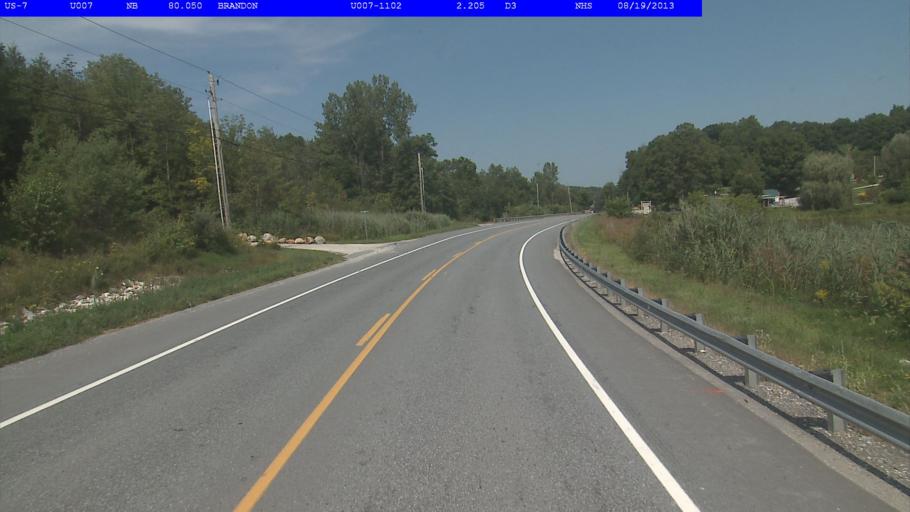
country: US
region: Vermont
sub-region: Rutland County
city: Brandon
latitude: 43.7831
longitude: -73.0630
